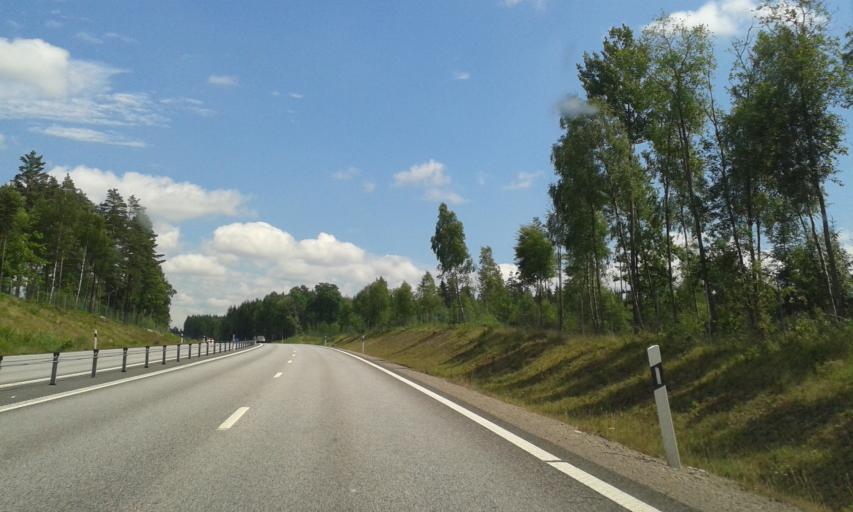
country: SE
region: Kronoberg
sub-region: Vaxjo Kommun
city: Gemla
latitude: 56.8964
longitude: 14.6912
